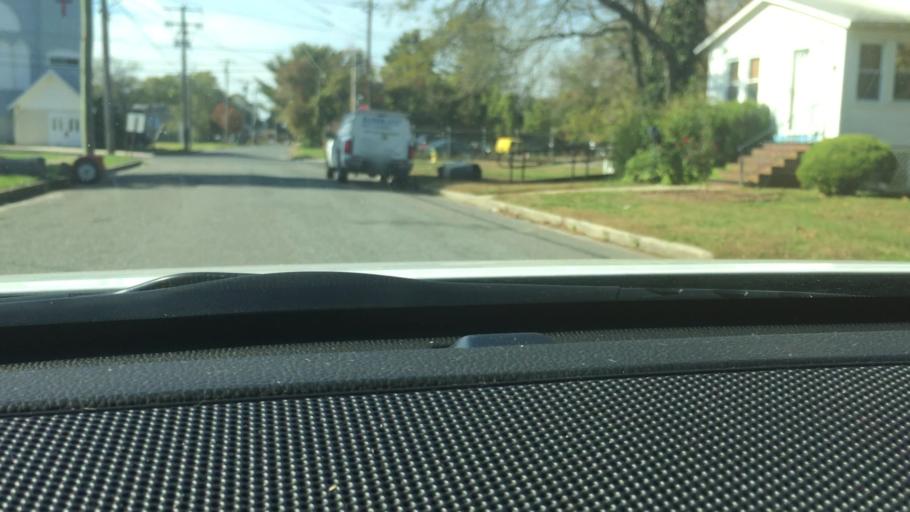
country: US
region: New Jersey
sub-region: Atlantic County
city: Pleasantville
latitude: 39.3906
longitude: -74.5343
